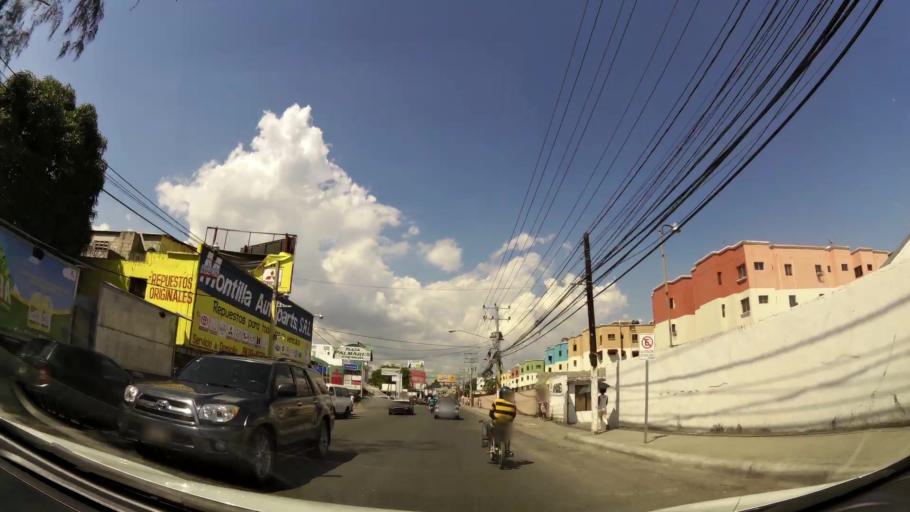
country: DO
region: Nacional
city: Bella Vista
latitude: 18.4583
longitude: -69.9770
